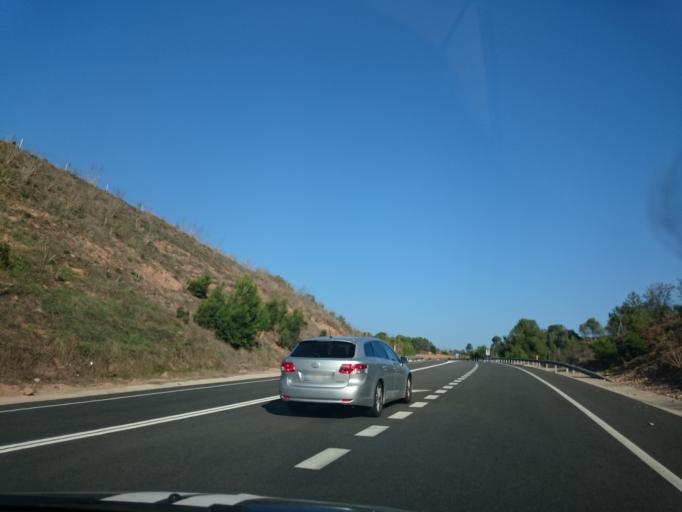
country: ES
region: Catalonia
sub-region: Provincia de Barcelona
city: Sant Salvador de Guardiola
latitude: 41.6771
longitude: 1.7547
